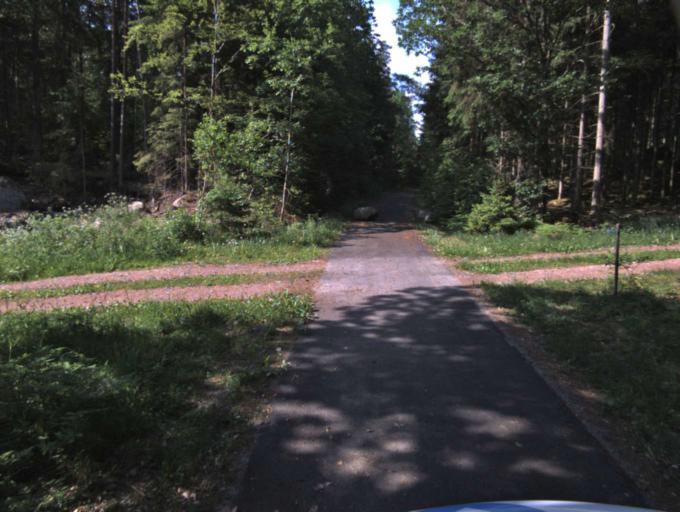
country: SE
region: Skane
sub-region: Kristianstads Kommun
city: Tollarp
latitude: 56.1978
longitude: 14.2587
